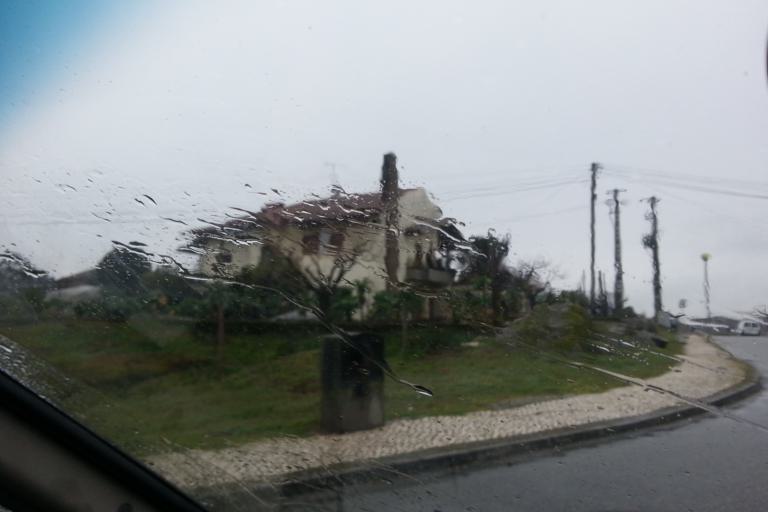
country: PT
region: Viseu
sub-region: Viseu
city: Rio de Loba
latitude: 40.6700
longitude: -7.8852
